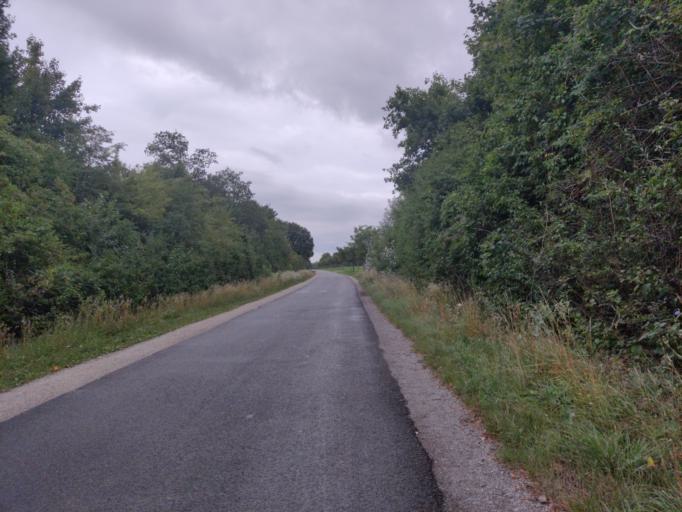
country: AT
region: Lower Austria
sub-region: Politischer Bezirk Korneuburg
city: Langenzersdorf
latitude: 48.2716
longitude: 16.3680
